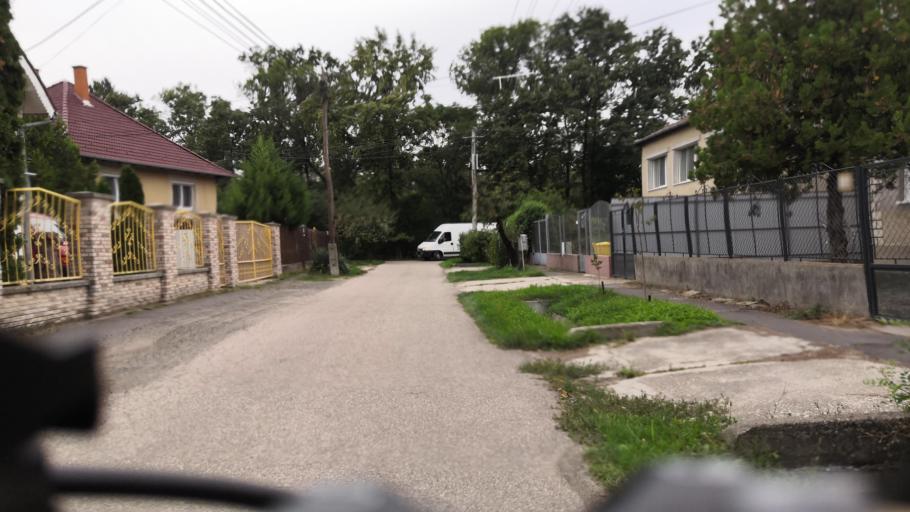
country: HU
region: Csongrad
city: Szeged
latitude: 46.2783
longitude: 20.1651
